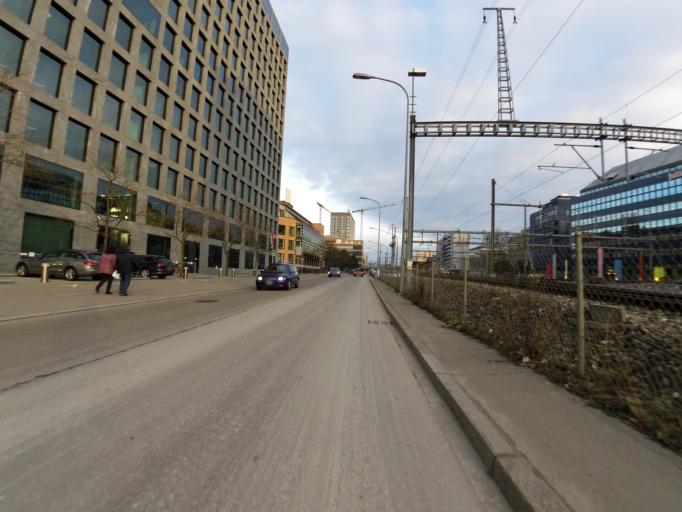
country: CH
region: Zurich
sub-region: Bezirk Zuerich
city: Zuerich (Kreis 9) / Altstetten
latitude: 47.3929
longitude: 8.4856
